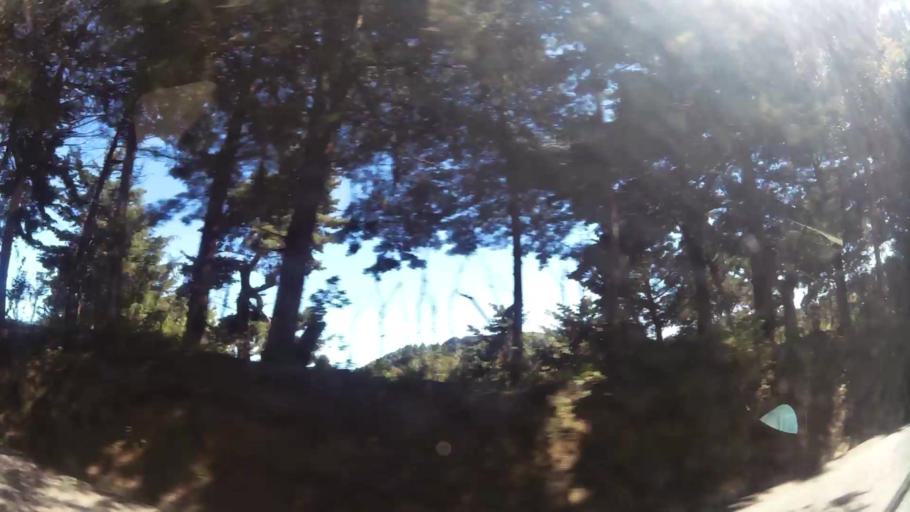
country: GT
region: Guatemala
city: San Jose Pinula
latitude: 14.5236
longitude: -90.4390
